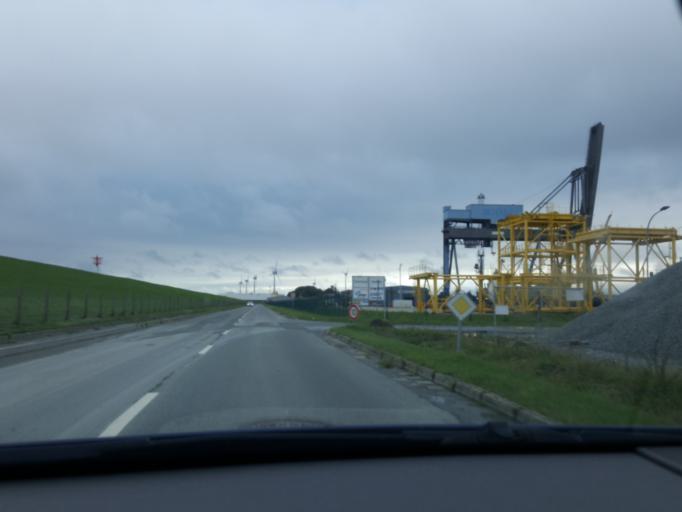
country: DE
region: Lower Saxony
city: Emden
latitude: 53.3341
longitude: 7.2041
